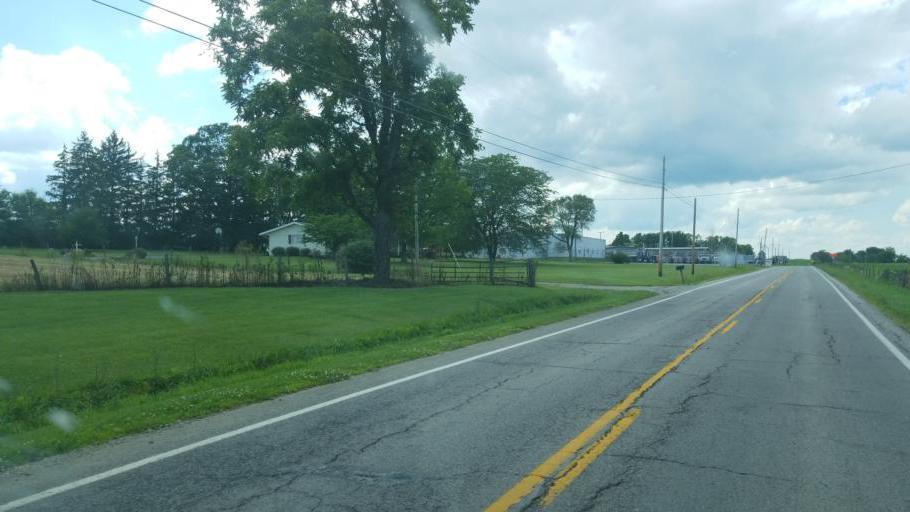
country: US
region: Ohio
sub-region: Highland County
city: Greenfield
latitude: 39.3791
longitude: -83.3832
